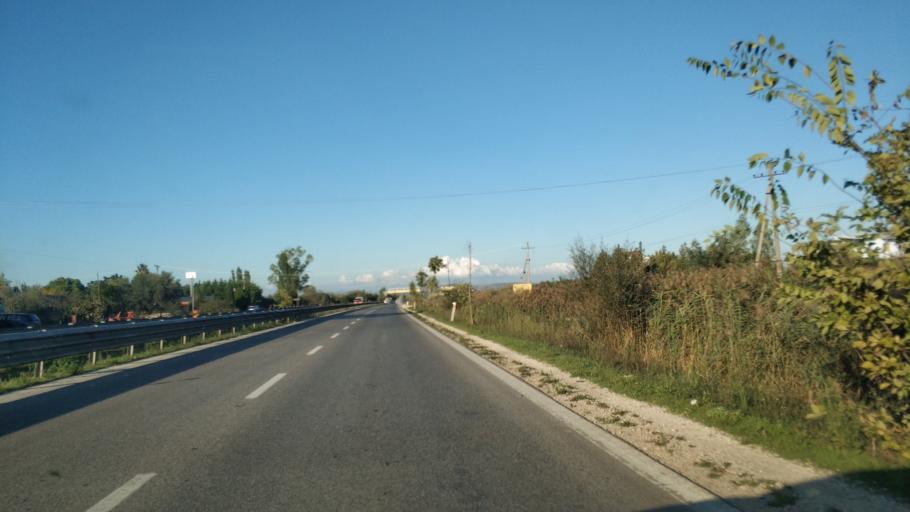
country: AL
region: Fier
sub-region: Rrethi i Lushnjes
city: Bubullime
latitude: 40.8546
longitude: 19.6437
